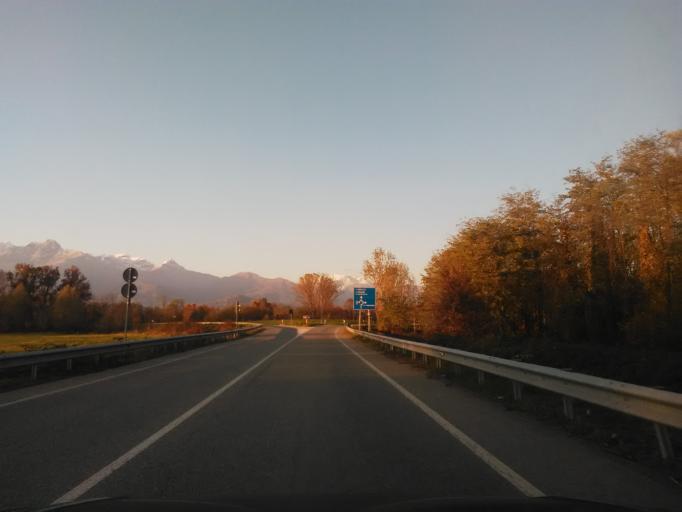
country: IT
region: Piedmont
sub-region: Provincia di Biella
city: Ponderano
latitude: 45.5238
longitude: 8.0487
